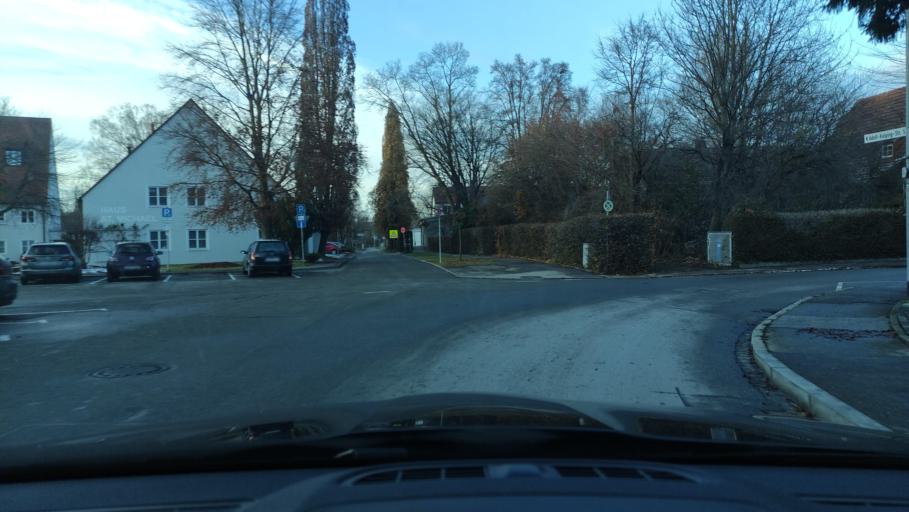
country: DE
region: Bavaria
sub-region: Swabia
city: Krumbach
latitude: 48.2458
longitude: 10.3641
